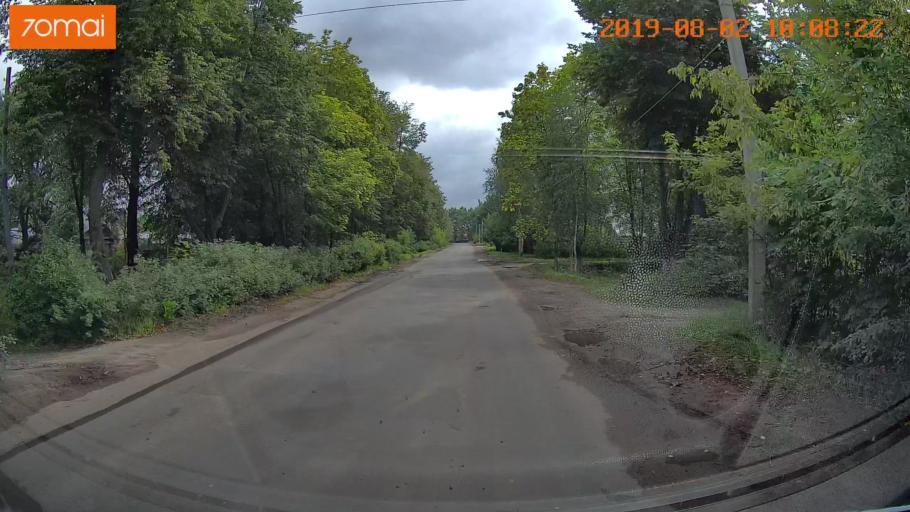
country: RU
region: Ivanovo
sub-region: Gorod Ivanovo
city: Ivanovo
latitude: 56.9853
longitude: 40.9392
